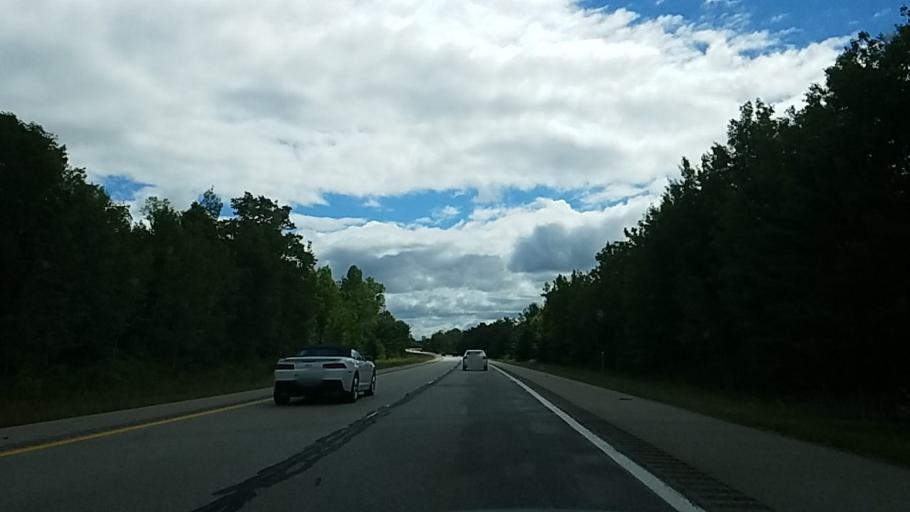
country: US
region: Michigan
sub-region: Ogemaw County
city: Skidway Lake
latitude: 44.0636
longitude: -84.0866
